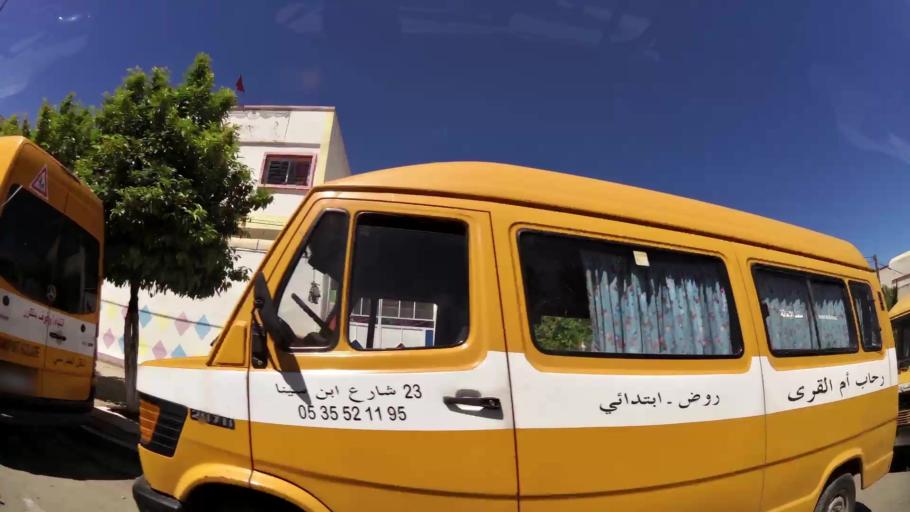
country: MA
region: Meknes-Tafilalet
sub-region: Meknes
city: Meknes
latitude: 33.9014
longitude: -5.5324
